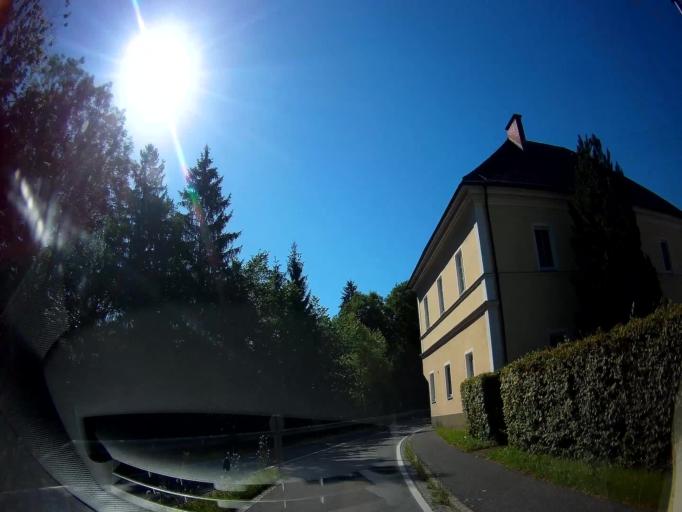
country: AT
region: Carinthia
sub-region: Politischer Bezirk Volkermarkt
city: Gallizien
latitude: 46.5583
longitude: 14.5096
